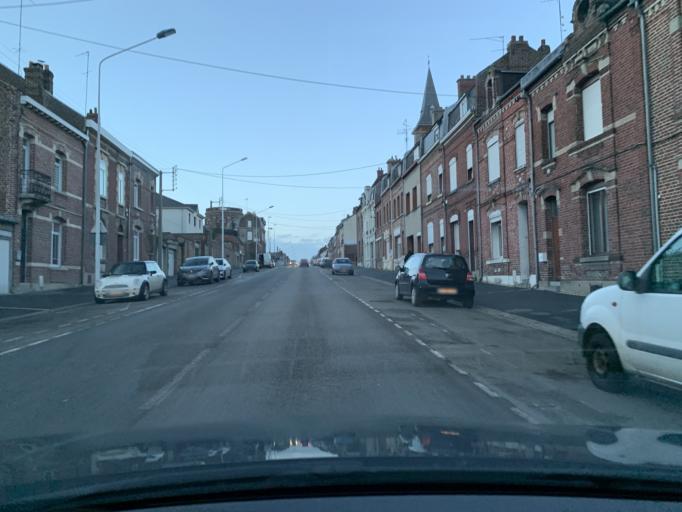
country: FR
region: Nord-Pas-de-Calais
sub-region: Departement du Nord
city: Cambrai
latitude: 50.1688
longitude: 3.2451
